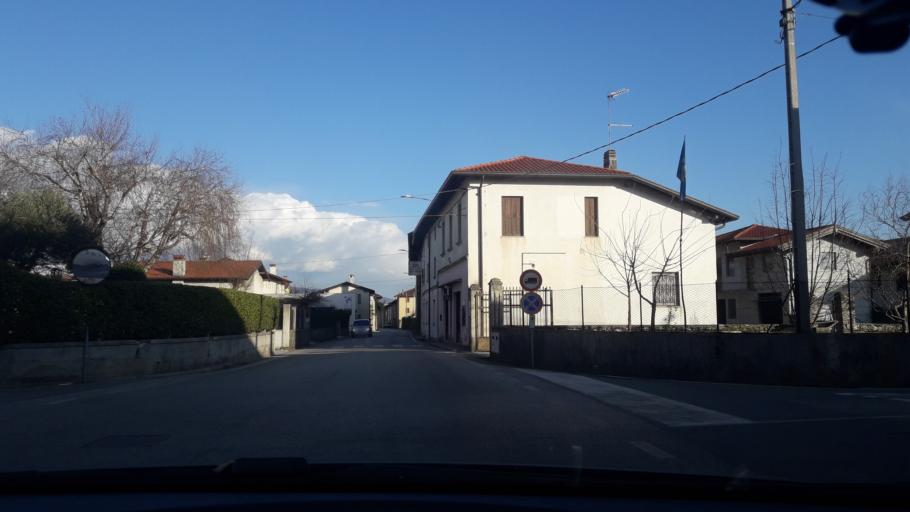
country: IT
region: Friuli Venezia Giulia
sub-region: Provincia di Udine
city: Reana del Roiale
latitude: 46.1443
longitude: 13.2333
